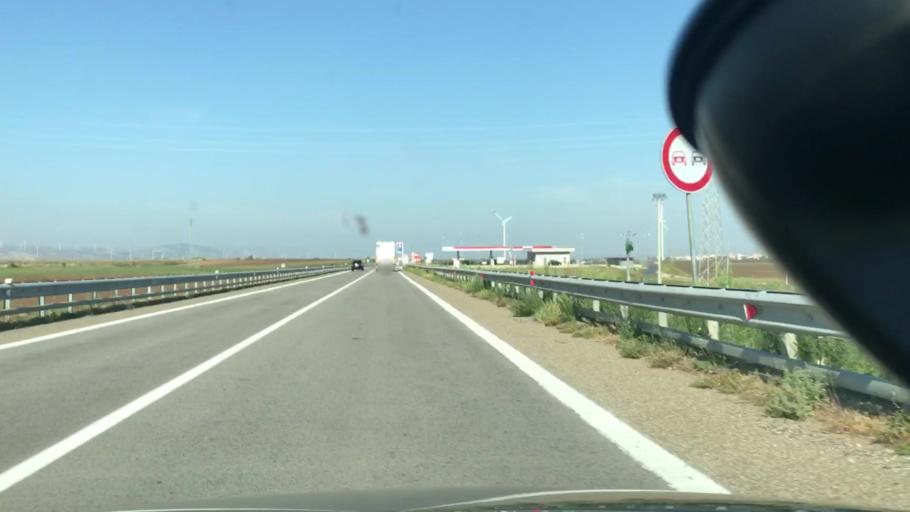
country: IT
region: Basilicate
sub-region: Provincia di Potenza
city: Lavello
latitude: 41.0166
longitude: 15.8185
